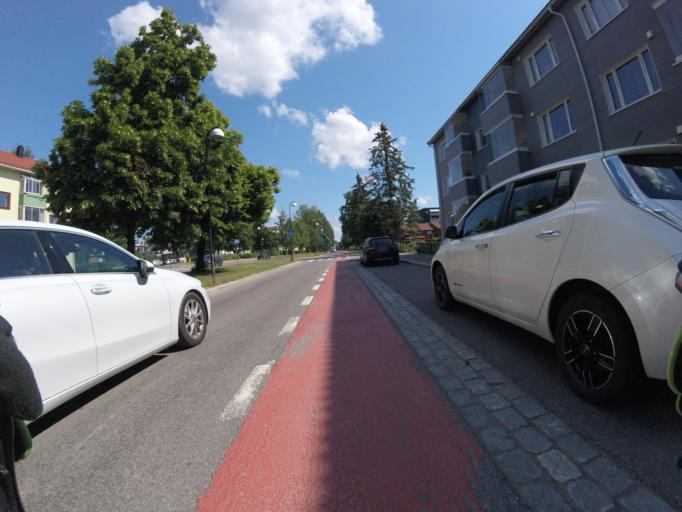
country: NO
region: Akershus
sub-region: Skedsmo
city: Lillestrom
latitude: 59.9593
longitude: 11.0557
